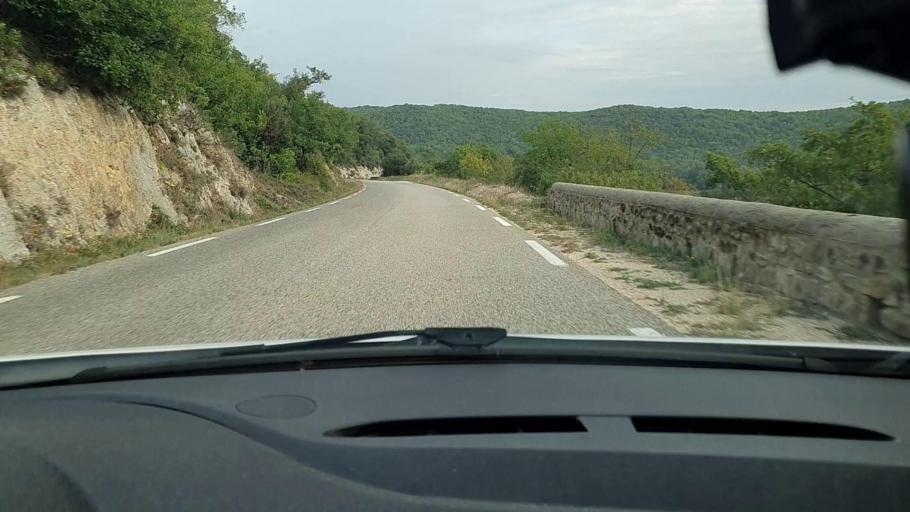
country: FR
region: Languedoc-Roussillon
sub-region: Departement du Gard
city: Barjac
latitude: 44.2382
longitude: 4.3042
